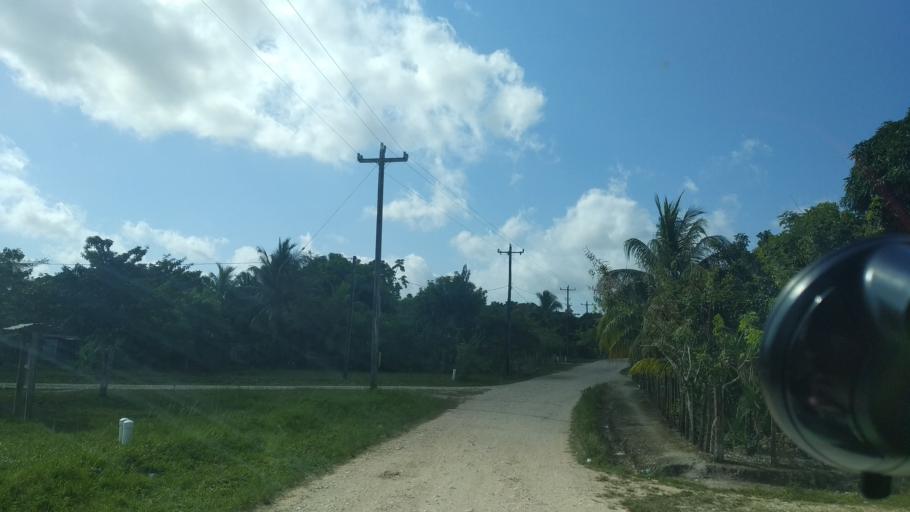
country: BZ
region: Stann Creek
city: Placencia
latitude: 16.4729
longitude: -88.6241
